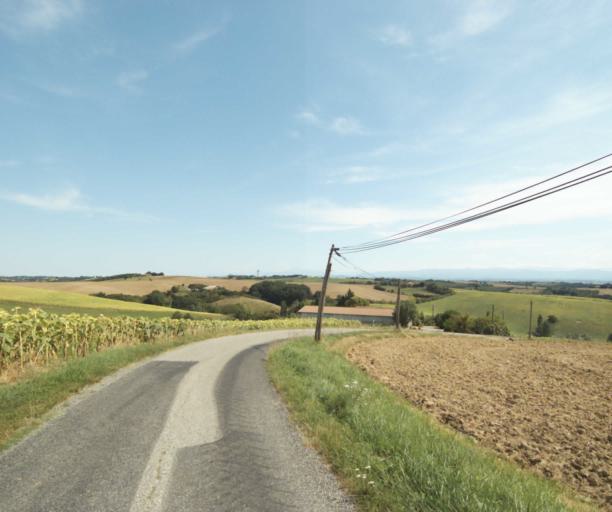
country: FR
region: Midi-Pyrenees
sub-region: Departement de la Haute-Garonne
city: Gaillac-Toulza
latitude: 43.2462
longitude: 1.4175
